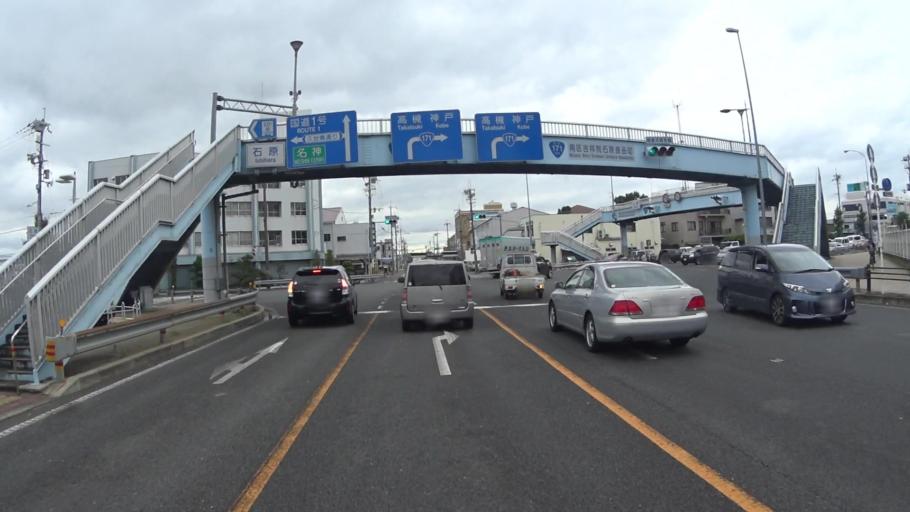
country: JP
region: Kyoto
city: Muko
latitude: 34.9666
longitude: 135.7266
